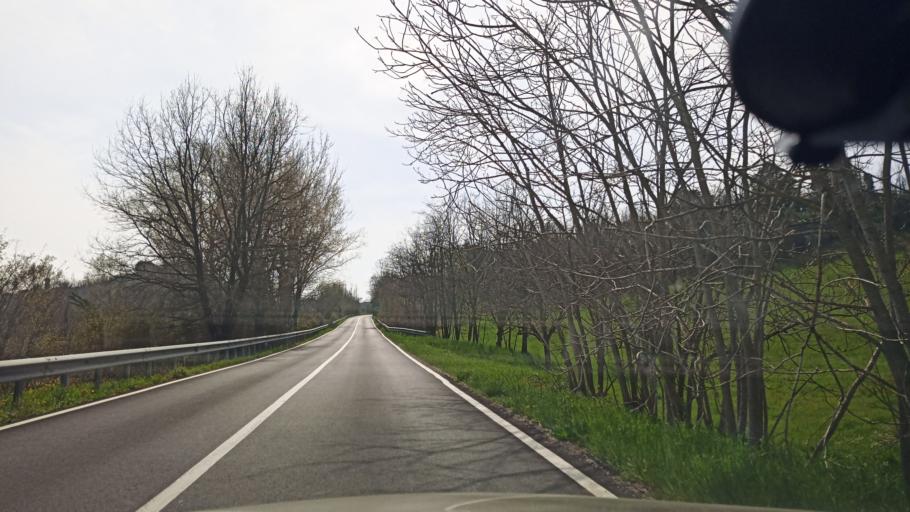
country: IT
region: Latium
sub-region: Provincia di Rieti
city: Cantalupo in Sabina
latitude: 42.3166
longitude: 12.6447
